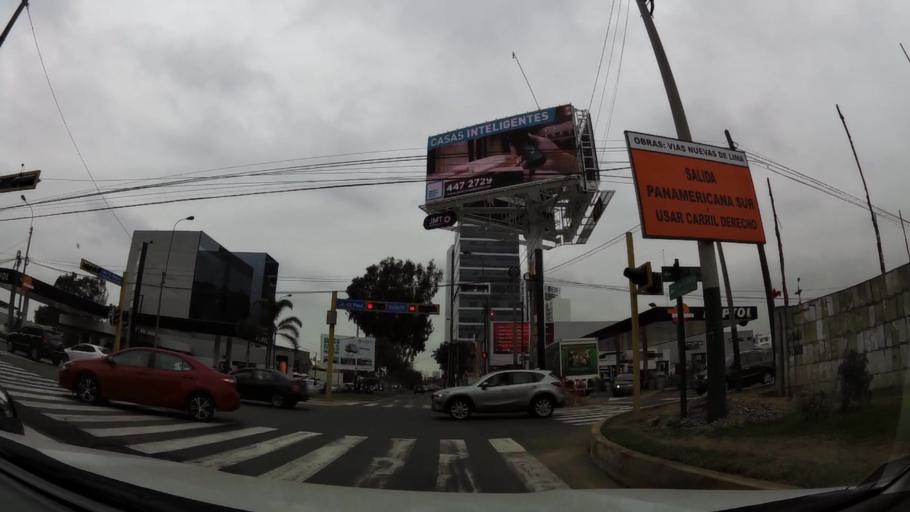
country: PE
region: Lima
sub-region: Lima
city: La Molina
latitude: -12.0988
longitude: -76.9705
